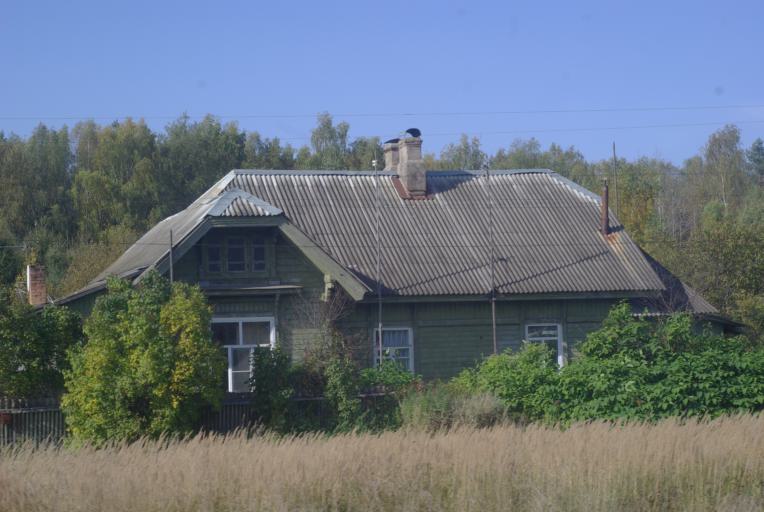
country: RU
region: Moskovskaya
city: Novo-Nikol'skoye
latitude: 56.5395
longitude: 37.5600
